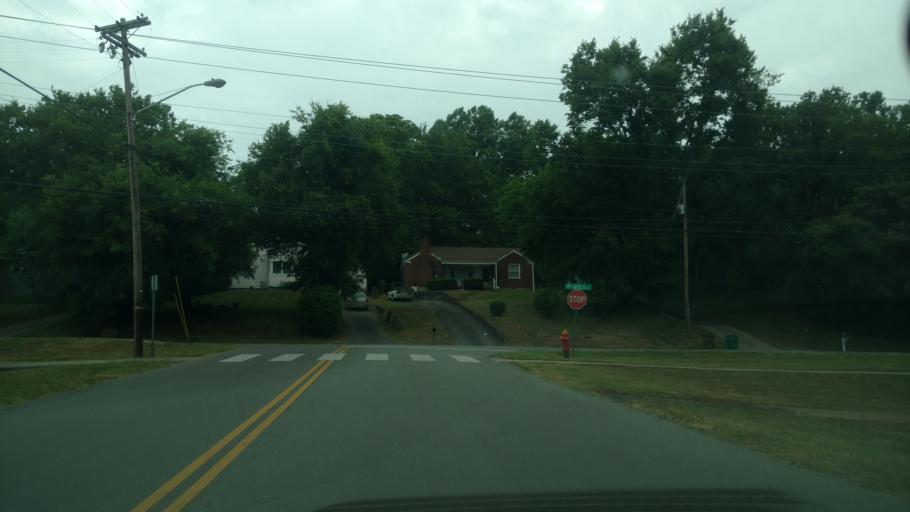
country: US
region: Tennessee
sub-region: Davidson County
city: Nashville
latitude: 36.2085
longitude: -86.7148
